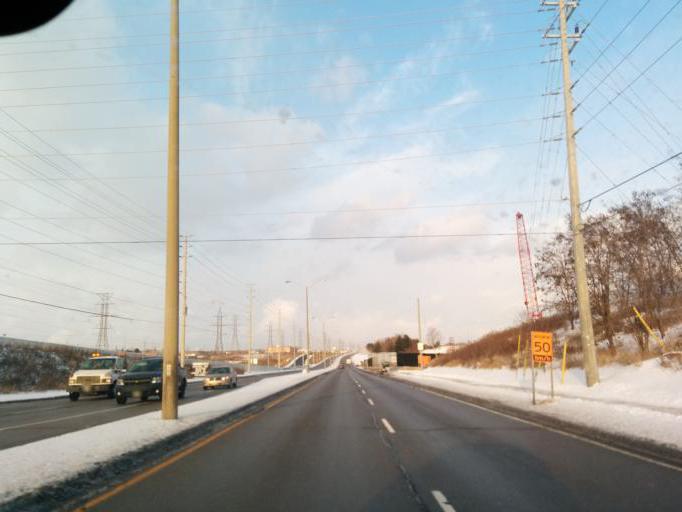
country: CA
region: Ontario
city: Mississauga
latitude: 43.6224
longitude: -79.6222
